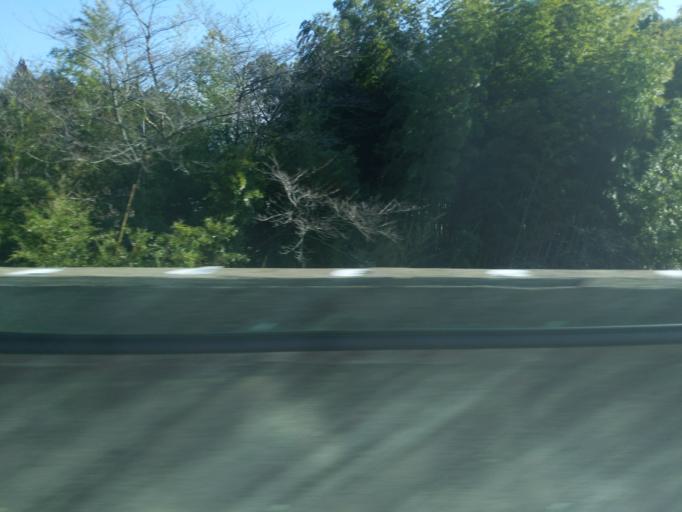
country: JP
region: Fukushima
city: Sukagawa
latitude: 37.3133
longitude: 140.3497
